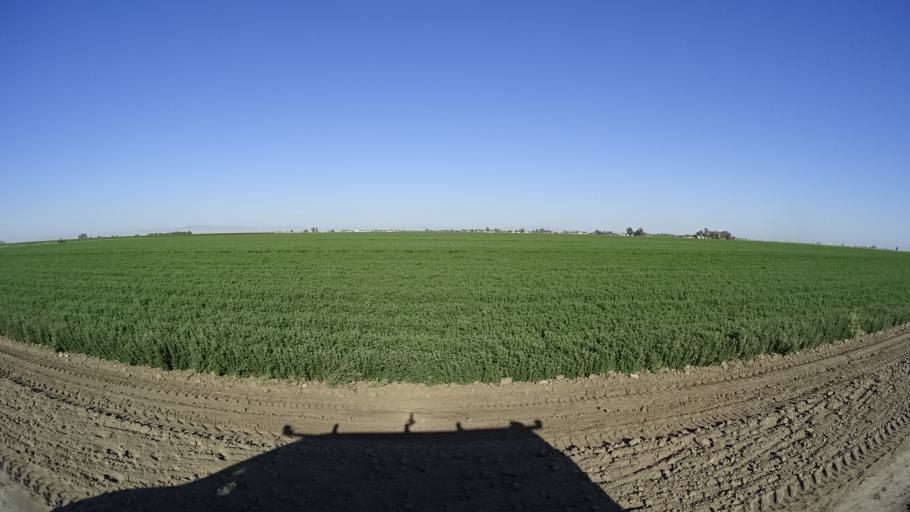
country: US
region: California
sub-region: Kings County
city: Stratford
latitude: 36.1844
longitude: -119.7983
